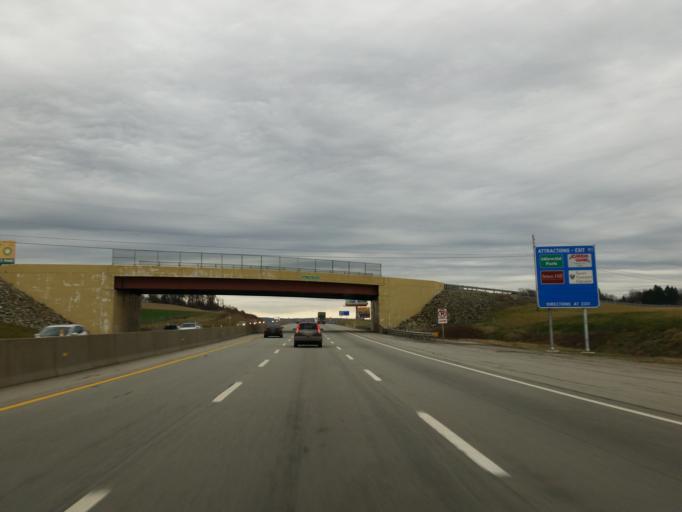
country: US
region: Pennsylvania
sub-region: Fayette County
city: Bear Rocks
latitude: 40.1268
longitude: -79.4057
